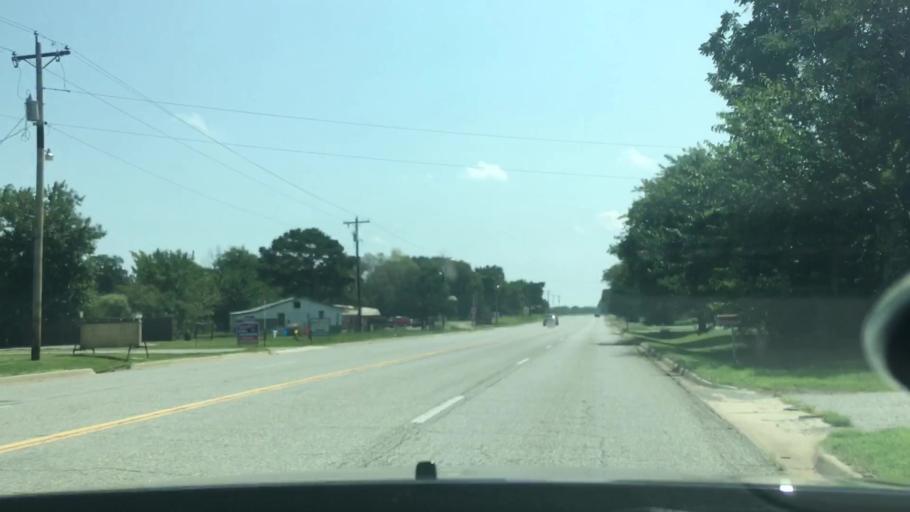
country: US
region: Oklahoma
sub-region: Atoka County
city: Atoka
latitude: 34.3002
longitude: -95.9916
